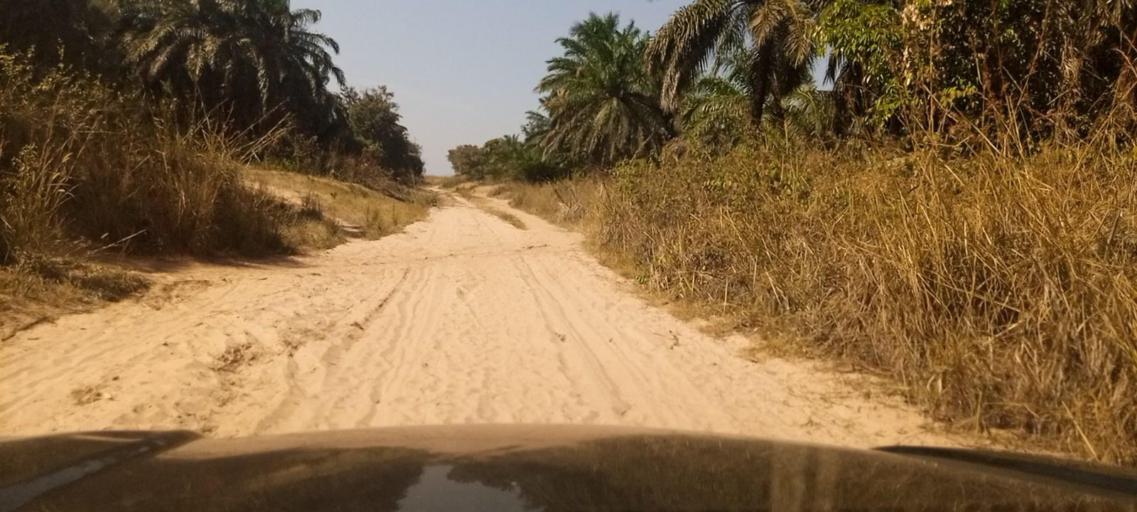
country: CD
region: Kasai-Oriental
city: Kabinda
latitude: -5.8042
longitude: 25.0257
